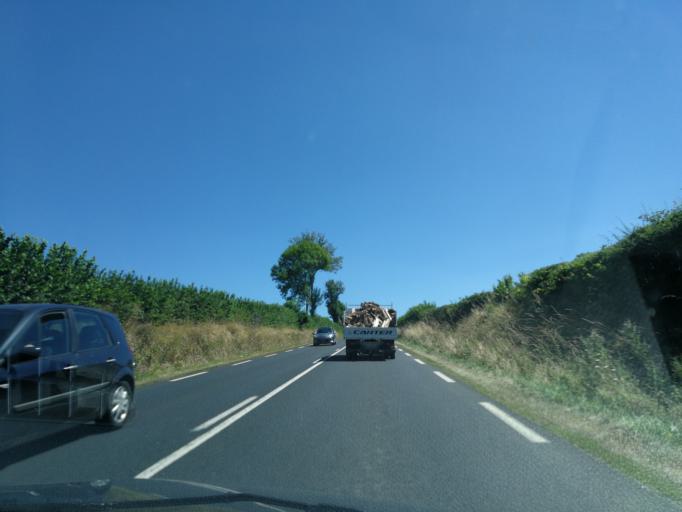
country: FR
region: Auvergne
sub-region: Departement du Cantal
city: Naucelles
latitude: 44.9355
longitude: 2.4001
